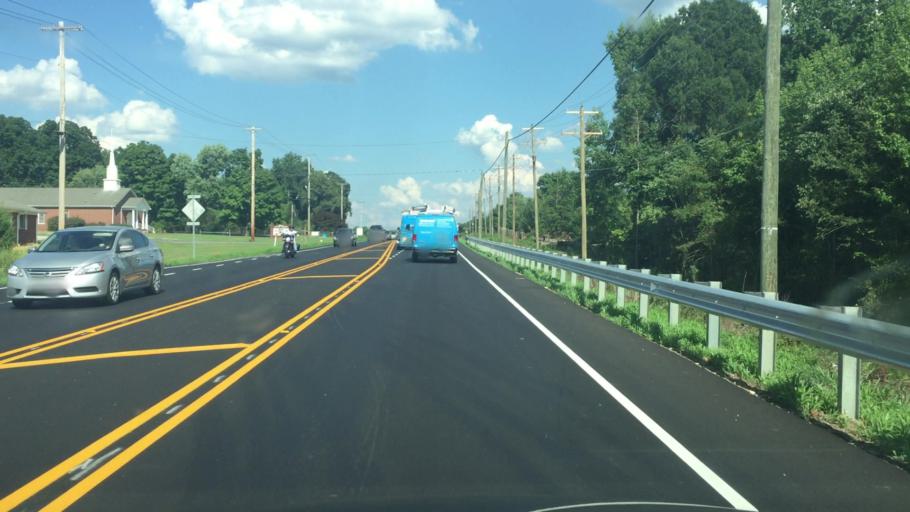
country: US
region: North Carolina
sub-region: Cabarrus County
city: Kannapolis
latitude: 35.4368
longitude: -80.6852
